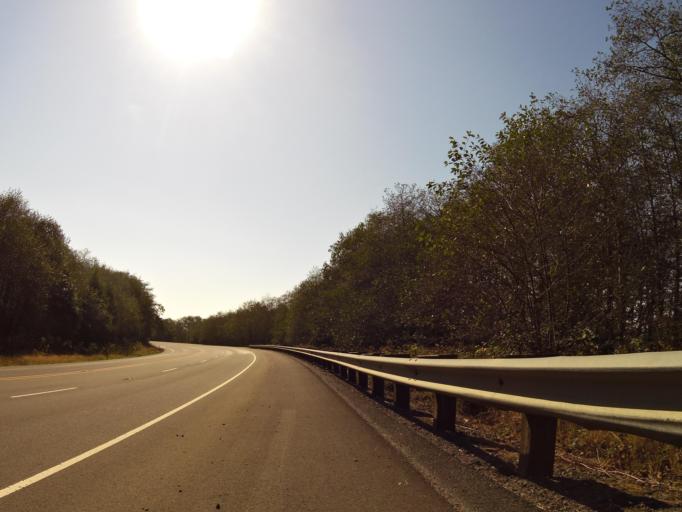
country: US
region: Oregon
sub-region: Tillamook County
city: Pacific City
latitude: 45.1459
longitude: -123.9675
